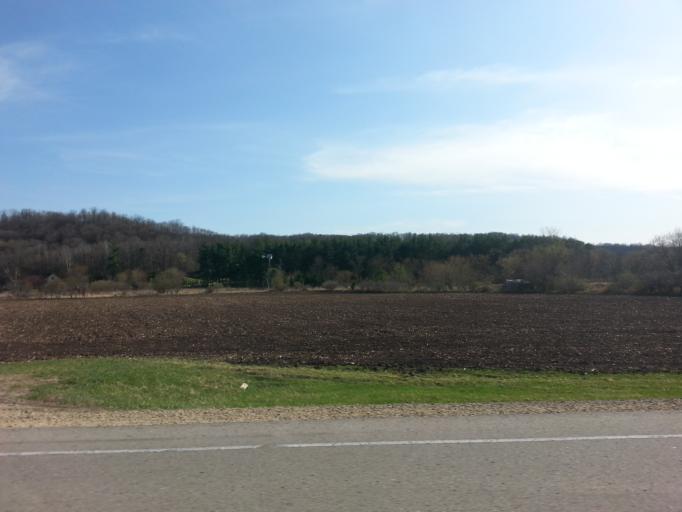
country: US
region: Wisconsin
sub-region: Pierce County
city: Ellsworth
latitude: 44.7758
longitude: -92.5141
